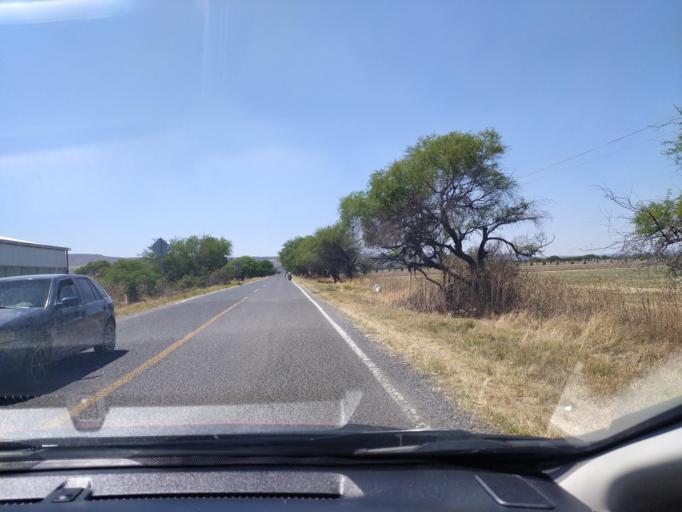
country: MX
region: Guanajuato
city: Ciudad Manuel Doblado
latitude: 20.7412
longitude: -101.9327
